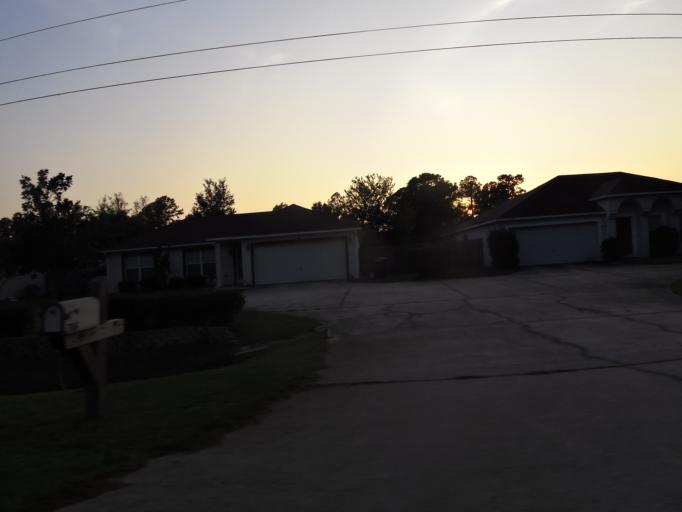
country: US
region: Florida
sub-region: Baker County
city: Macclenny
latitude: 30.2924
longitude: -82.1244
